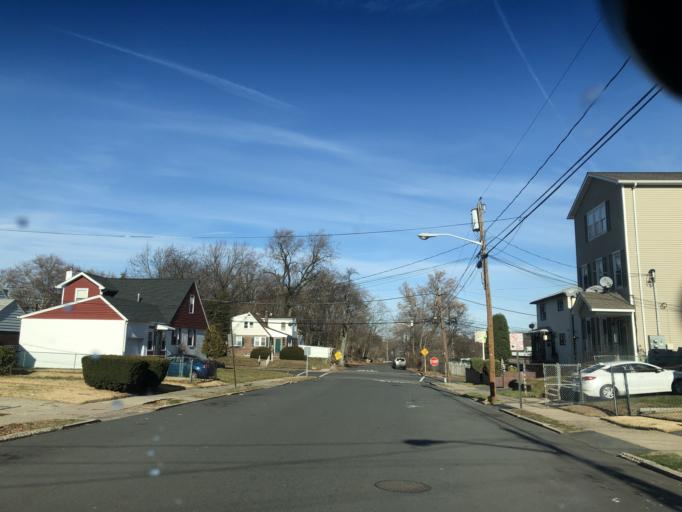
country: US
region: New Jersey
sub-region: Bergen County
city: Fair Lawn
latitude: 40.9254
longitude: -74.1439
